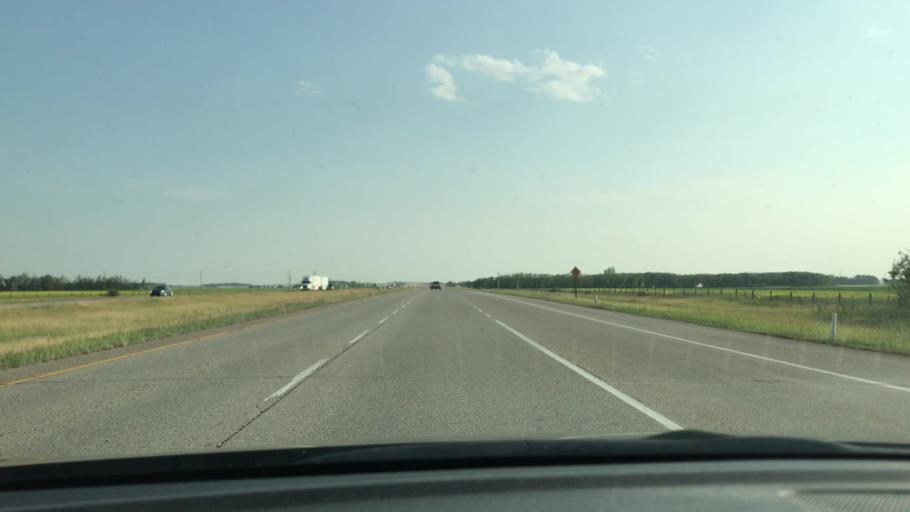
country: CA
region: Alberta
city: Leduc
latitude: 53.2263
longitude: -113.5761
